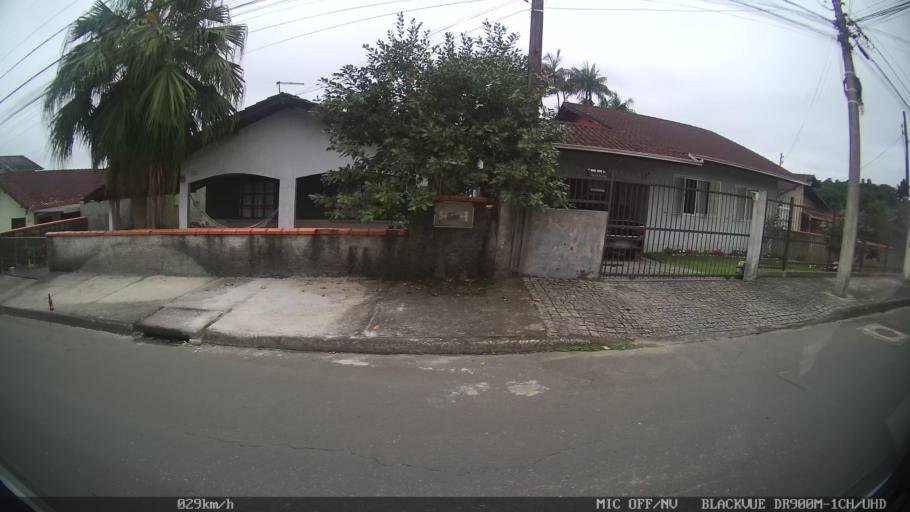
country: BR
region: Santa Catarina
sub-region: Joinville
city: Joinville
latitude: -26.2700
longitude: -48.8866
